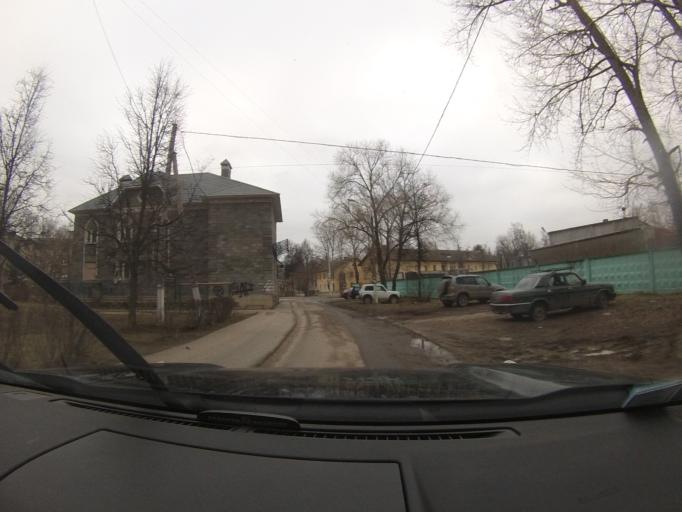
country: RU
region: Moskovskaya
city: Peski
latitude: 55.2509
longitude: 38.7641
